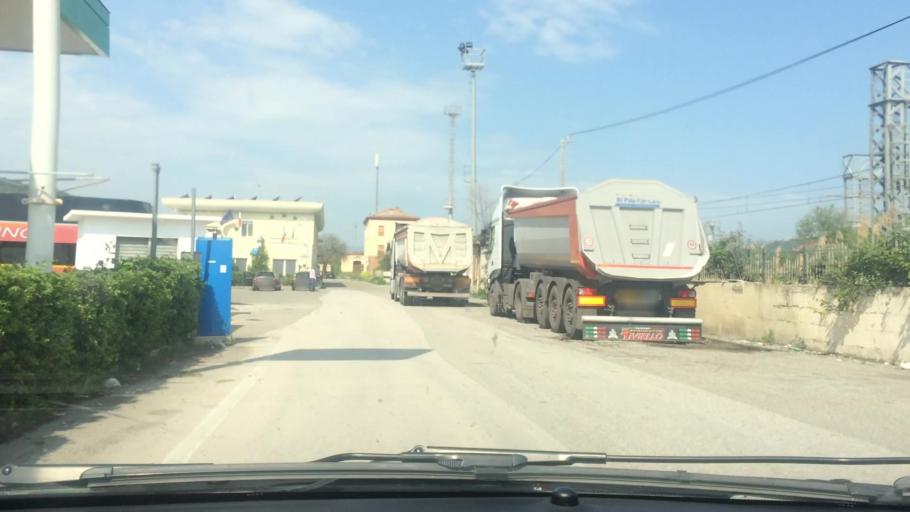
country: IT
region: Basilicate
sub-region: Provincia di Matera
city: Grottole
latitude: 40.5830
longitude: 16.3532
